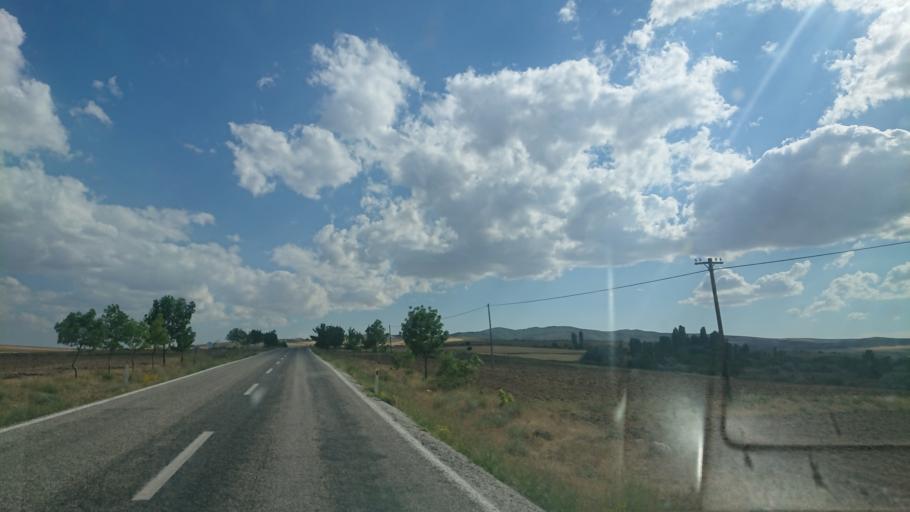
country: TR
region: Aksaray
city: Sariyahsi
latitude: 38.9457
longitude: 33.8374
